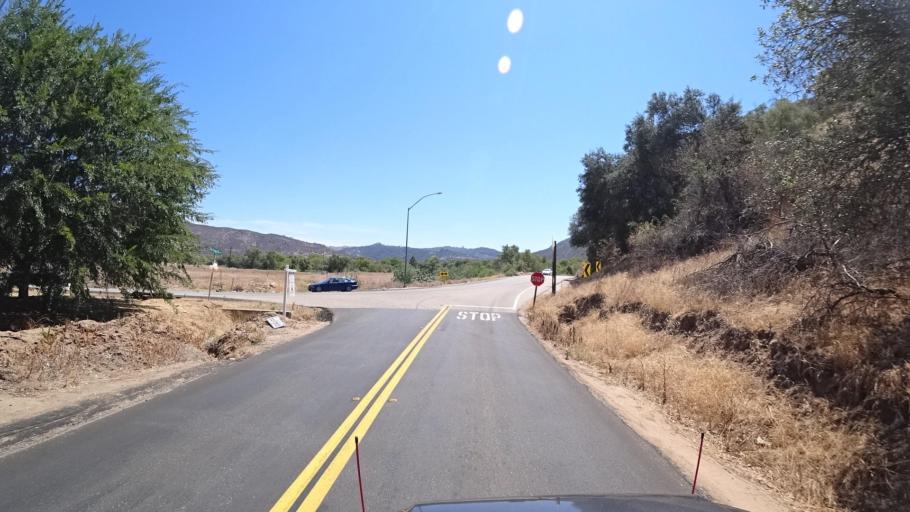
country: US
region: California
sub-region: San Diego County
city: Rainbow
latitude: 33.3431
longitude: -117.1332
